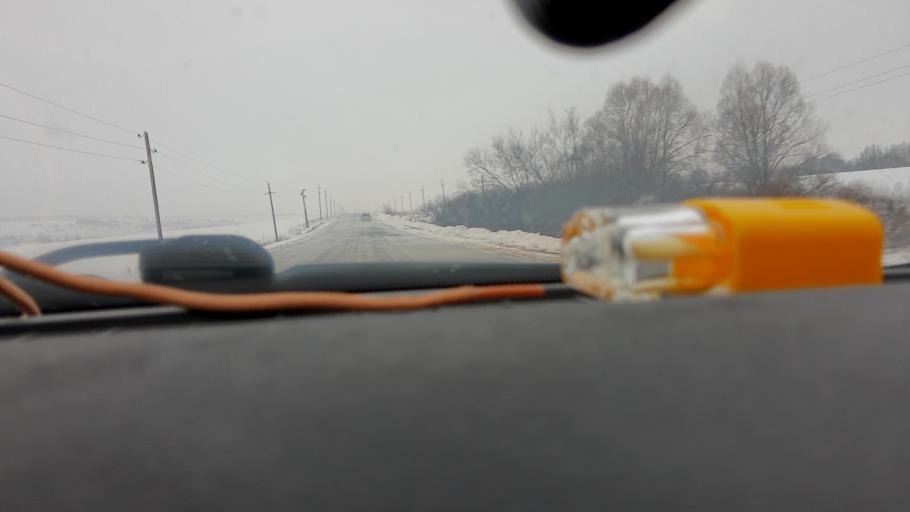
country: RU
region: Bashkortostan
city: Ulukulevo
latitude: 54.5435
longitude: 56.4328
